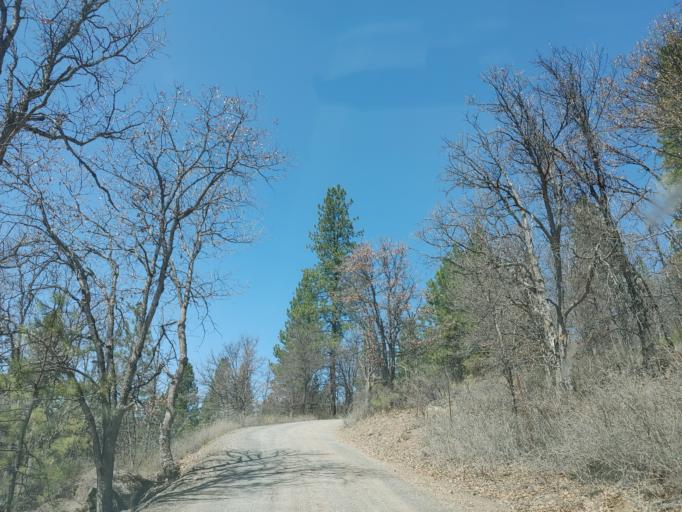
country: US
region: California
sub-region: Shasta County
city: Burney
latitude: 41.0184
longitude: -121.6209
